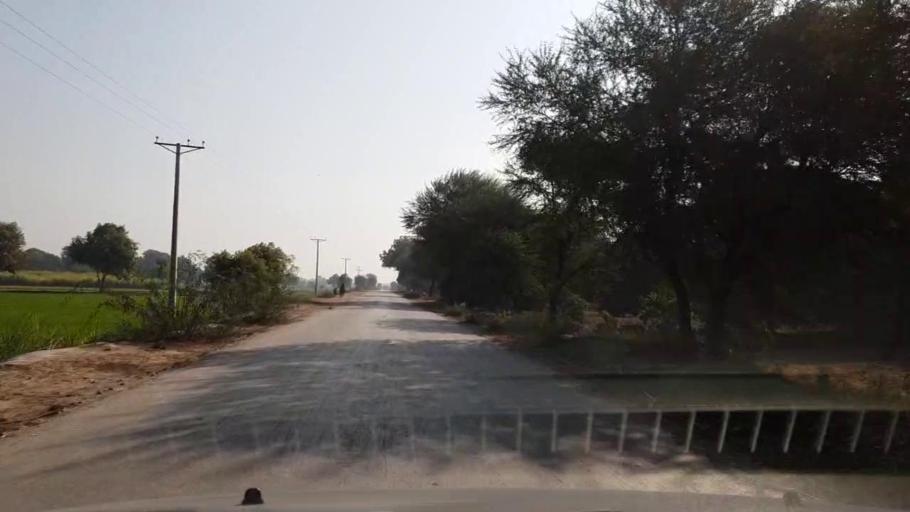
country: PK
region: Sindh
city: Tando Jam
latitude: 25.5228
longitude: 68.5953
